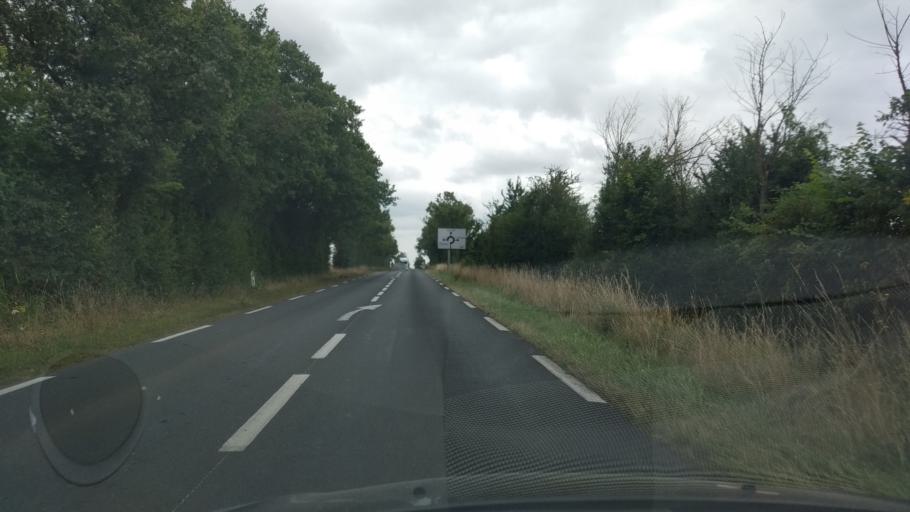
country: FR
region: Poitou-Charentes
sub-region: Departement de la Vienne
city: Roches-Premarie-Andille
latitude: 46.4975
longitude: 0.3649
